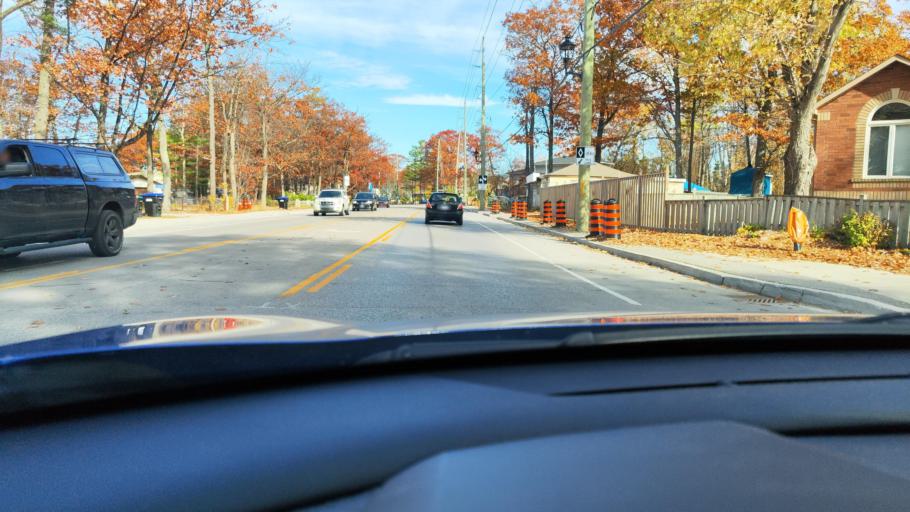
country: CA
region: Ontario
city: Wasaga Beach
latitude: 44.4915
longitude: -80.0456
